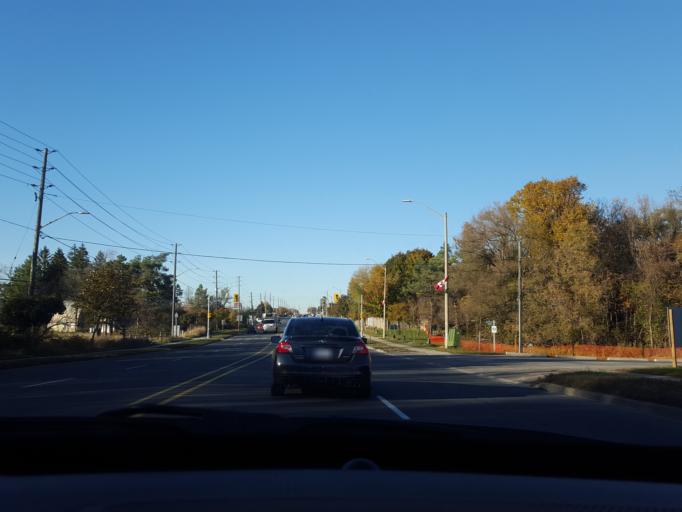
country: CA
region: Ontario
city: Markham
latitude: 43.8627
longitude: -79.2834
